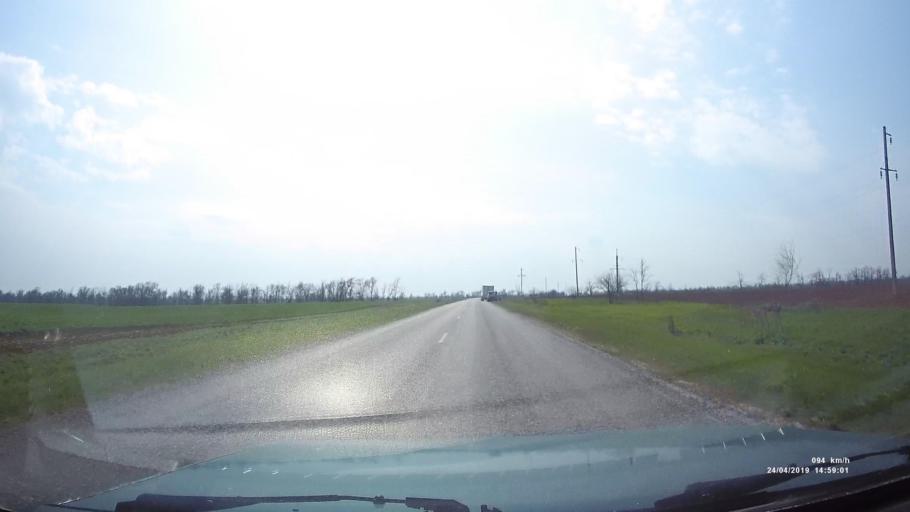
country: RU
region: Rostov
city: Remontnoye
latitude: 46.5675
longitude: 43.5826
